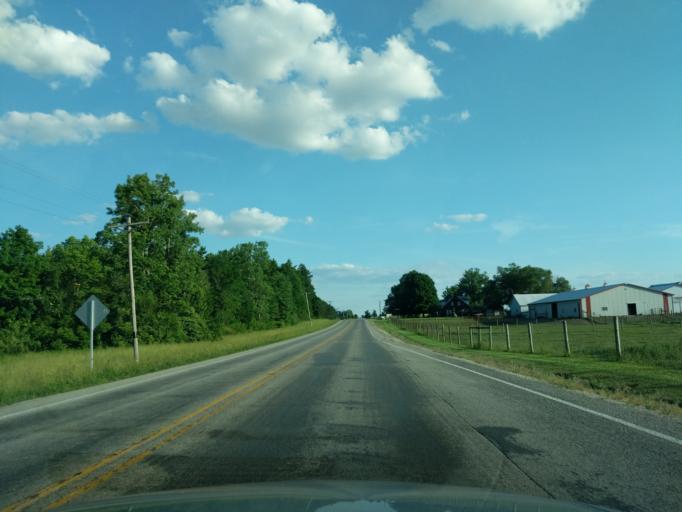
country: US
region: Indiana
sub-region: Huntington County
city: Huntington
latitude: 40.8352
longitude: -85.4654
